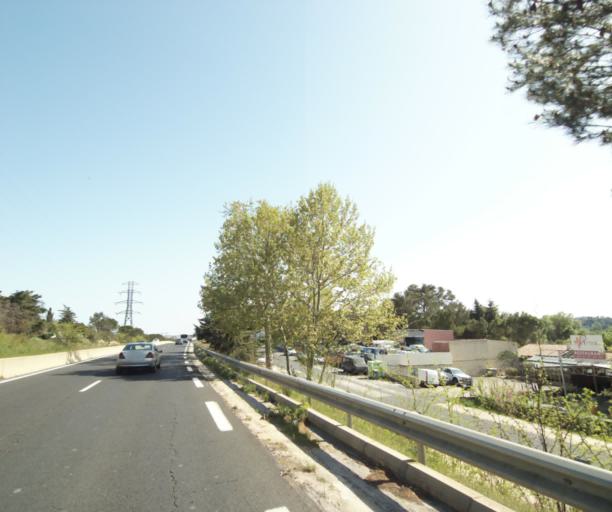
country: FR
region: Languedoc-Roussillon
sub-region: Departement de l'Herault
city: Montferrier-sur-Lez
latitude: 43.6503
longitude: 3.8388
